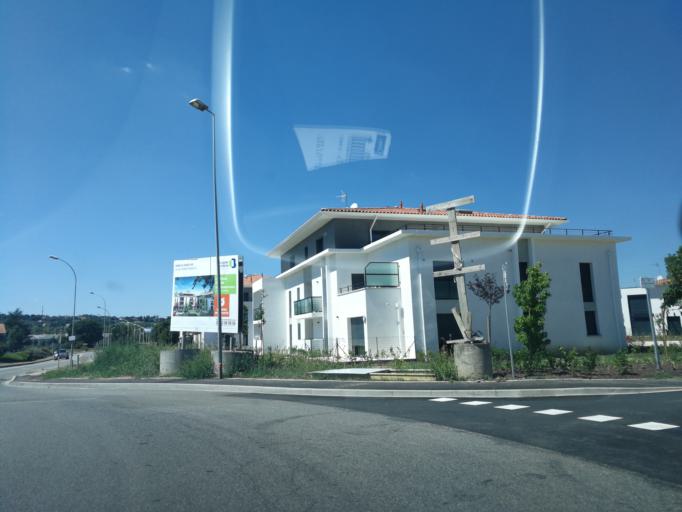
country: FR
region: Midi-Pyrenees
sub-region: Departement de la Haute-Garonne
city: Balma
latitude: 43.5966
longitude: 1.5015
